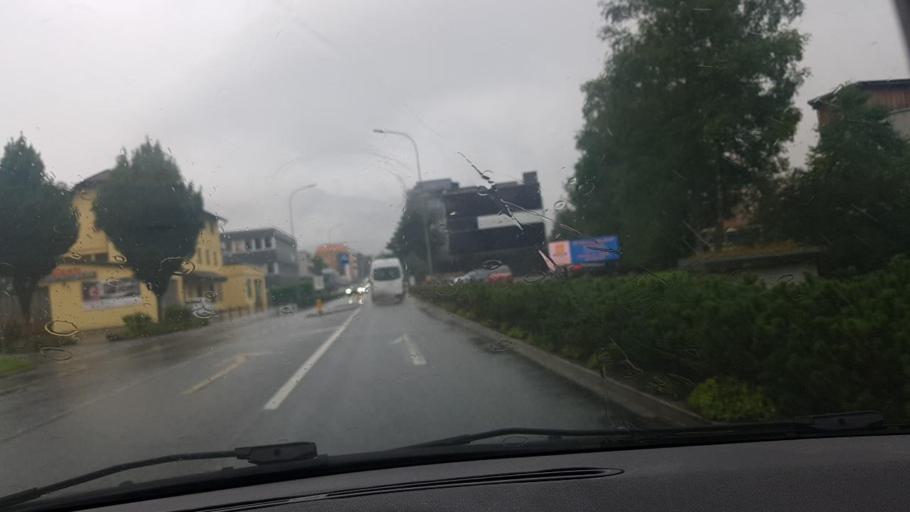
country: LI
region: Balzers
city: Balzers
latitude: 47.0778
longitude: 9.5132
